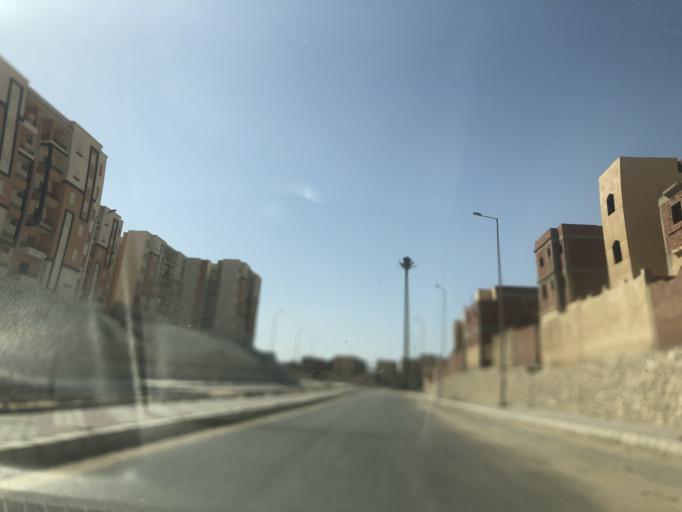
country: EG
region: Al Jizah
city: Madinat Sittah Uktubar
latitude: 29.9350
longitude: 30.9796
